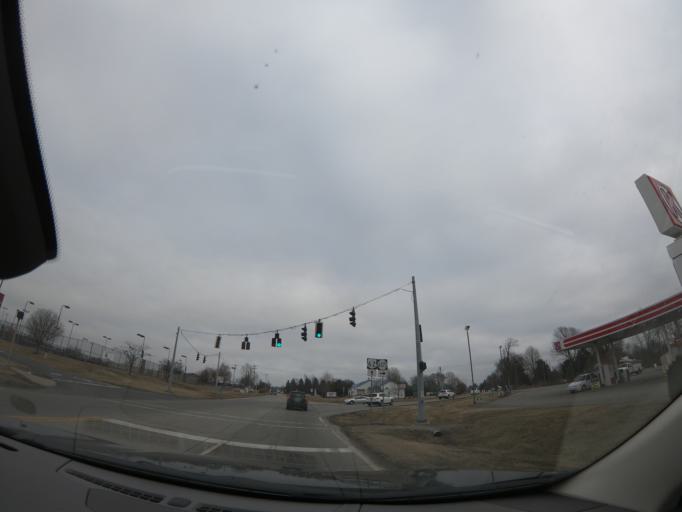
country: US
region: Kentucky
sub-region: Nelson County
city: Bardstown
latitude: 37.8279
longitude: -85.4233
